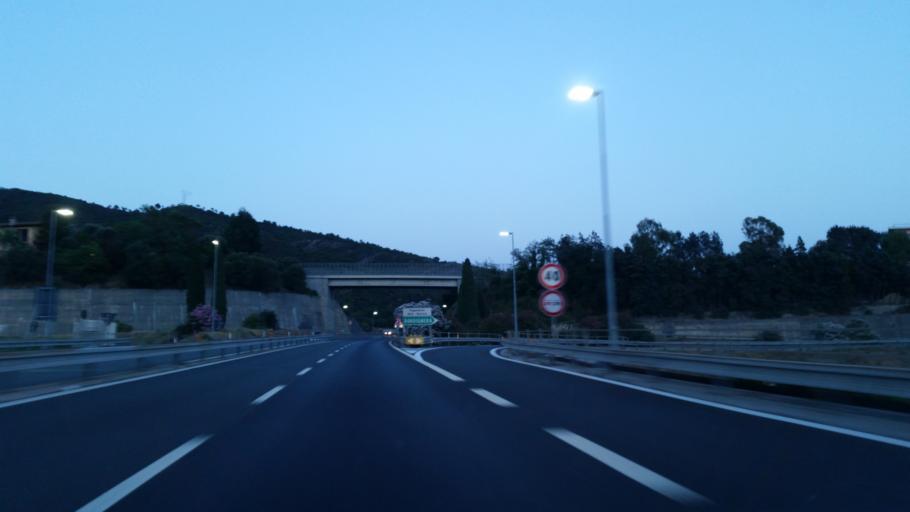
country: IT
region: Liguria
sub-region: Provincia di Imperia
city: Vallebona
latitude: 43.7998
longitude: 7.6665
